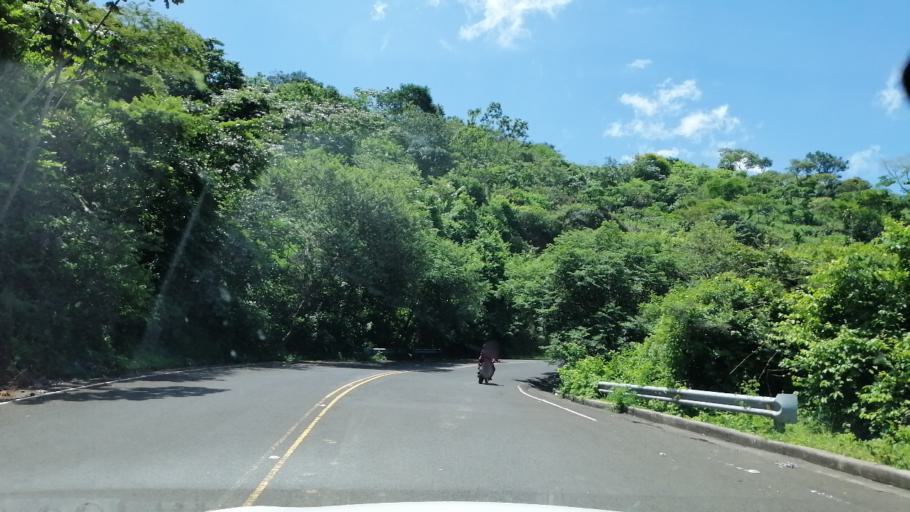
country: SV
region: San Miguel
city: Ciudad Barrios
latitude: 13.7953
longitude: -88.2916
